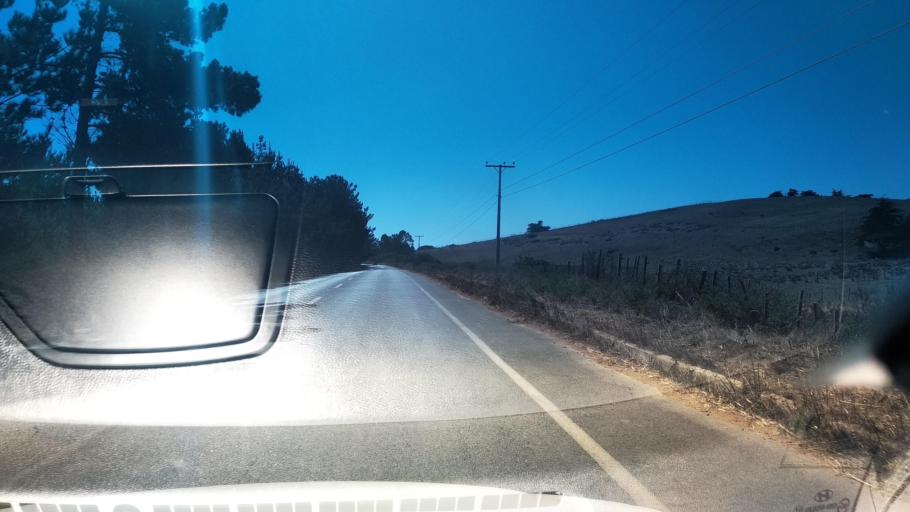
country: CL
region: O'Higgins
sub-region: Provincia de Colchagua
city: Santa Cruz
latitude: -34.4611
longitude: -72.0243
